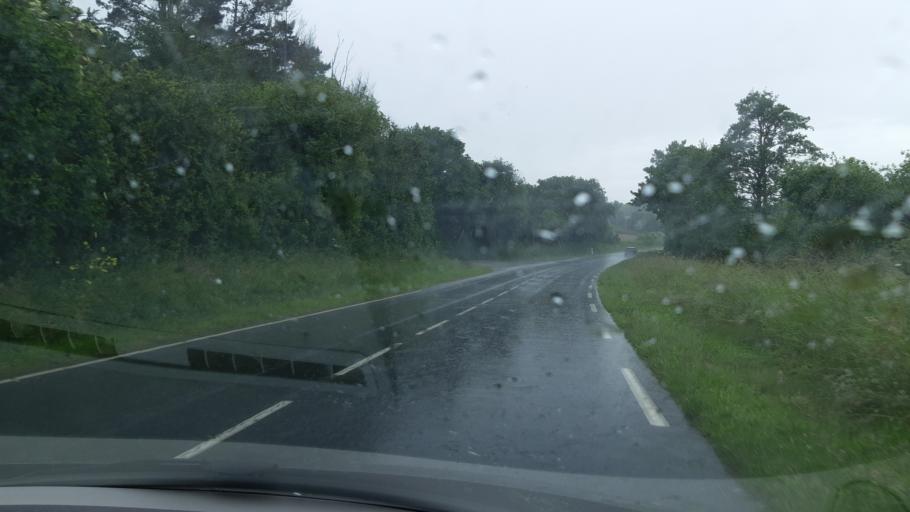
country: FR
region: Brittany
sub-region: Departement du Finistere
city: Plougoulm
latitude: 48.6584
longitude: -4.0248
